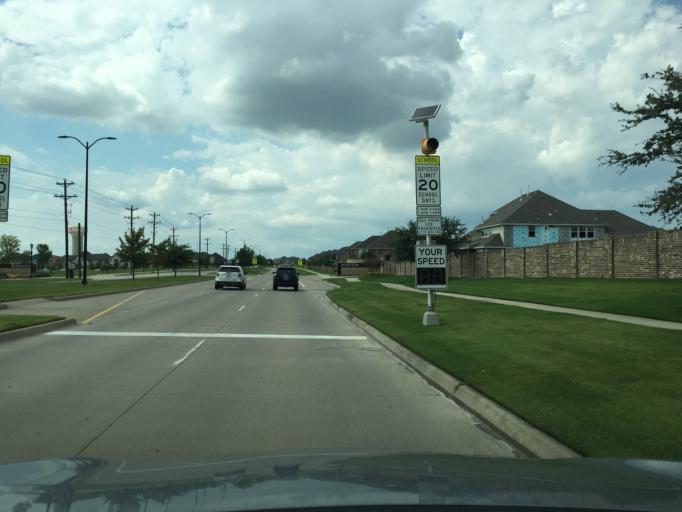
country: US
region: Texas
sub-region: Denton County
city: The Colony
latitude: 33.1383
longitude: -96.8791
